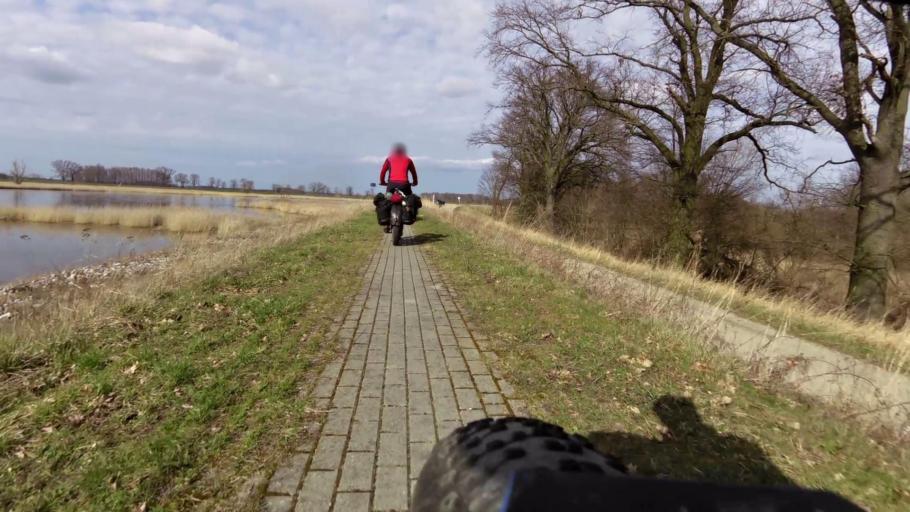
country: DE
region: Brandenburg
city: Reitwein
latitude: 52.4727
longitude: 14.6137
